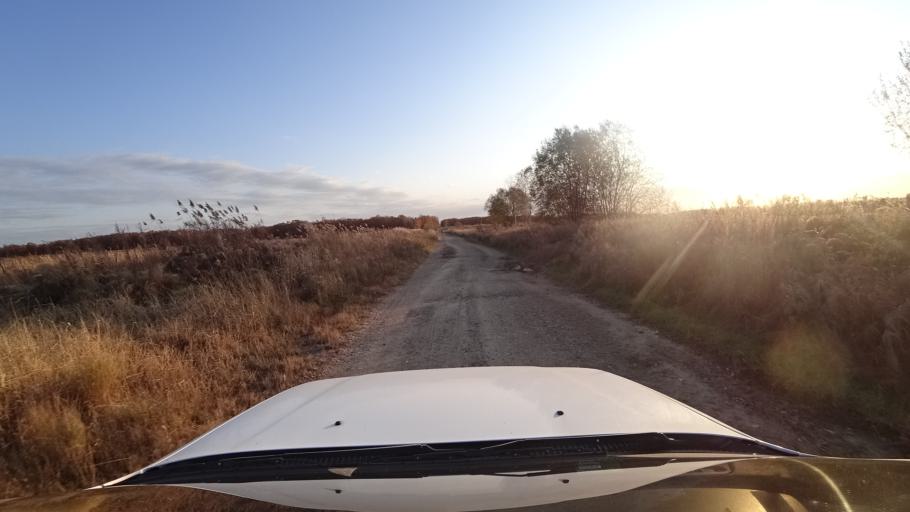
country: RU
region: Primorskiy
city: Lazo
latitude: 45.8097
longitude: 133.6074
